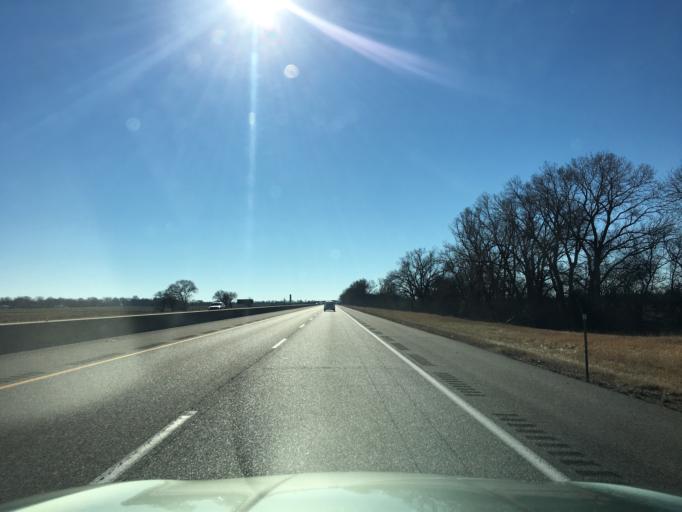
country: US
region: Kansas
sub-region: Sumner County
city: Belle Plaine
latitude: 37.4468
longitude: -97.3221
